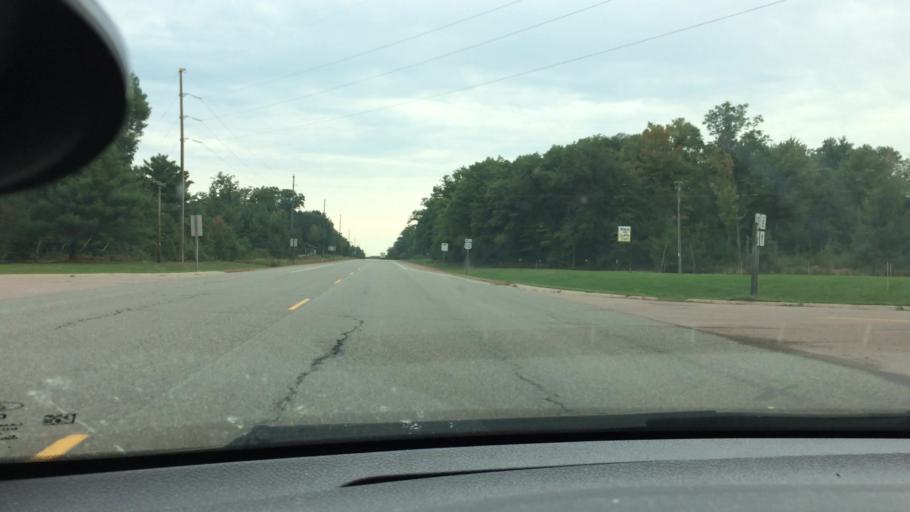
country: US
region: Wisconsin
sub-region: Clark County
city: Neillsville
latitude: 44.5727
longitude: -90.7302
